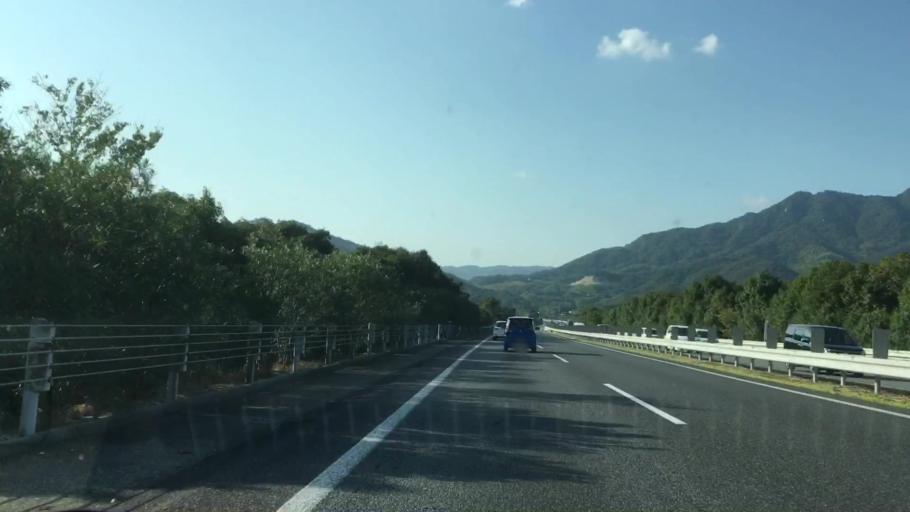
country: JP
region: Yamaguchi
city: Hofu
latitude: 34.0622
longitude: 131.6085
